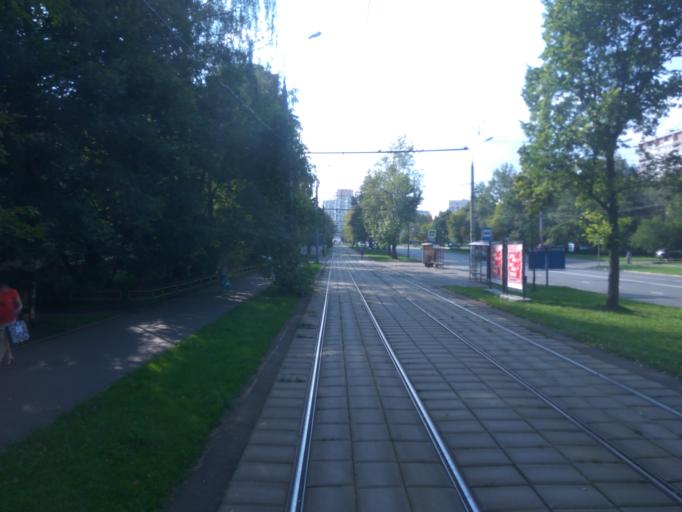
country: RU
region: Moskovskaya
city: Novogireyevo
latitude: 55.7527
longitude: 37.8088
